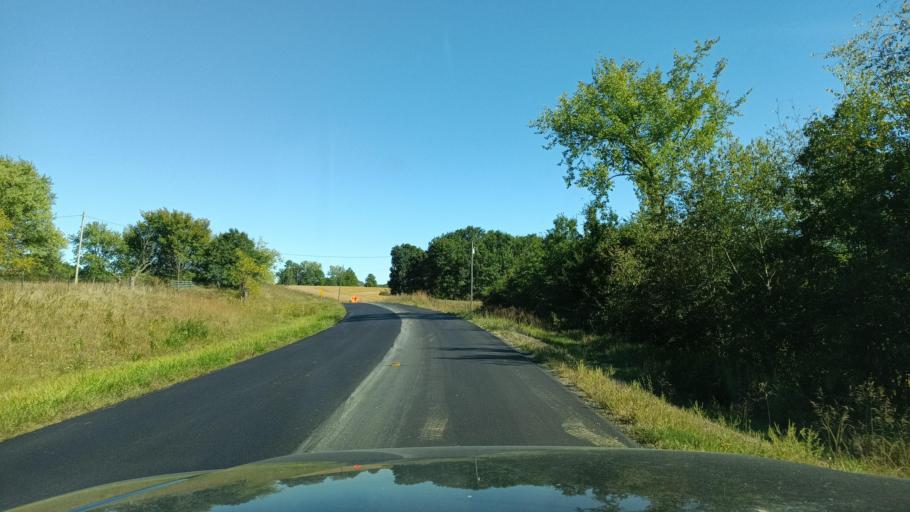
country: US
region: Missouri
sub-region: Macon County
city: La Plata
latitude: 39.9198
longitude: -92.5290
